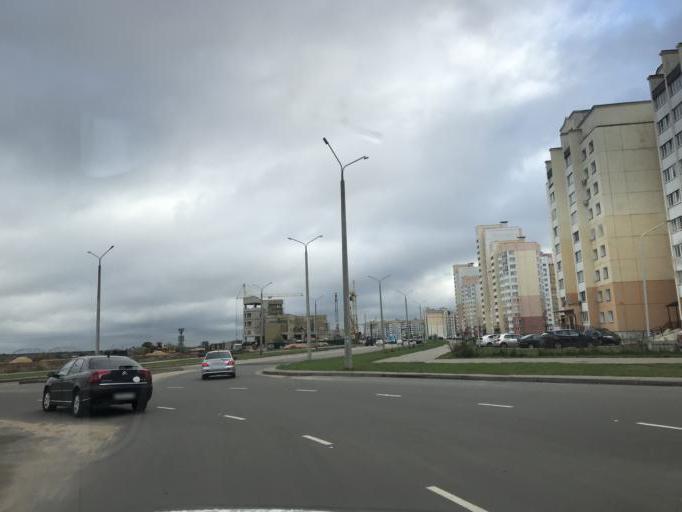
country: BY
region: Mogilev
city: Mahilyow
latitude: 53.8824
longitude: 30.3569
